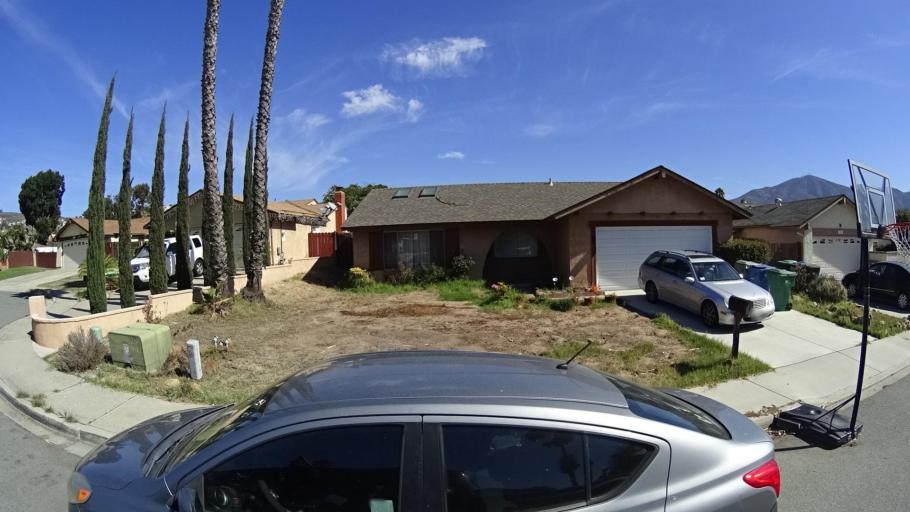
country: US
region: California
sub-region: San Diego County
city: La Presa
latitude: 32.7071
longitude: -116.9896
